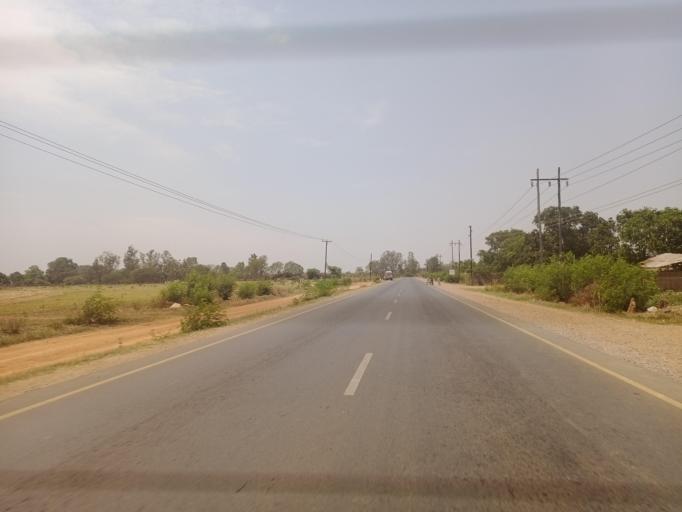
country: ZM
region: Lusaka
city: Lusaka
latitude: -15.2744
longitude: 28.4055
